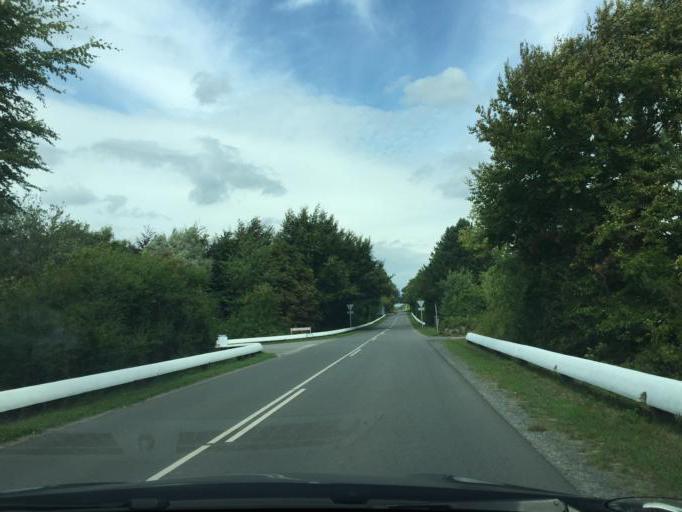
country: DK
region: South Denmark
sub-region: Assens Kommune
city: Tommerup Stationsby
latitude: 55.3885
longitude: 10.1959
